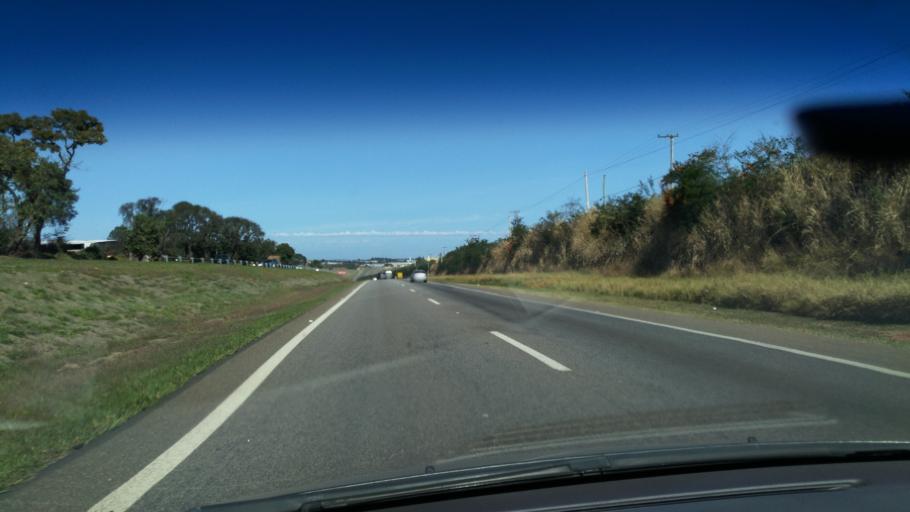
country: BR
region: Sao Paulo
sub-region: Jaguariuna
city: Jaguariuna
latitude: -22.6471
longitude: -47.0057
